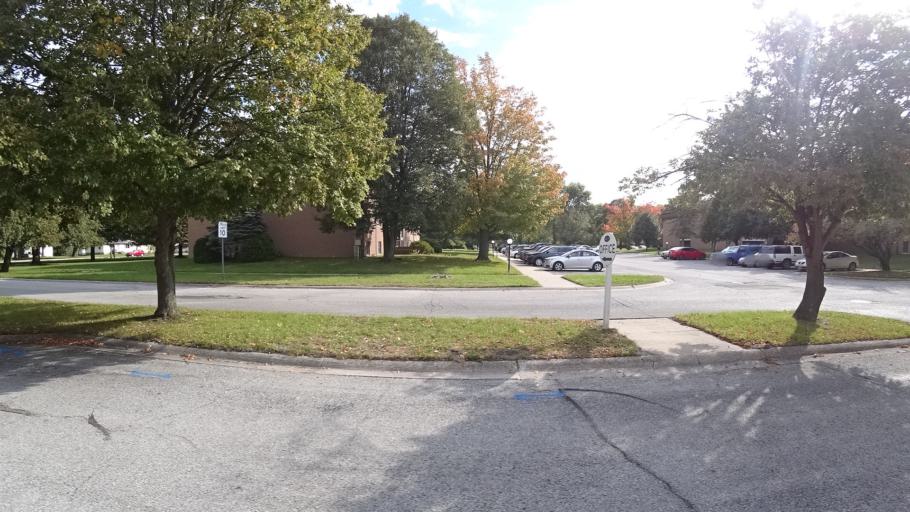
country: US
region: Indiana
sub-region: LaPorte County
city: Trail Creek
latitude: 41.6941
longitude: -86.8659
